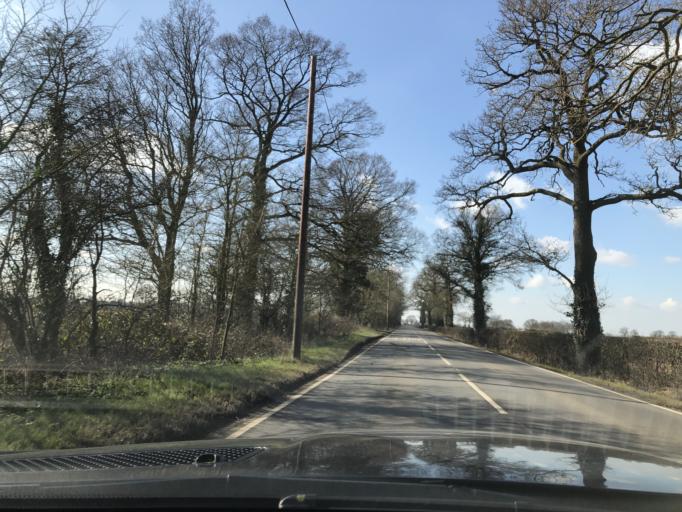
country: GB
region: England
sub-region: Warwickshire
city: Wolston
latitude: 52.3378
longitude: -1.3602
